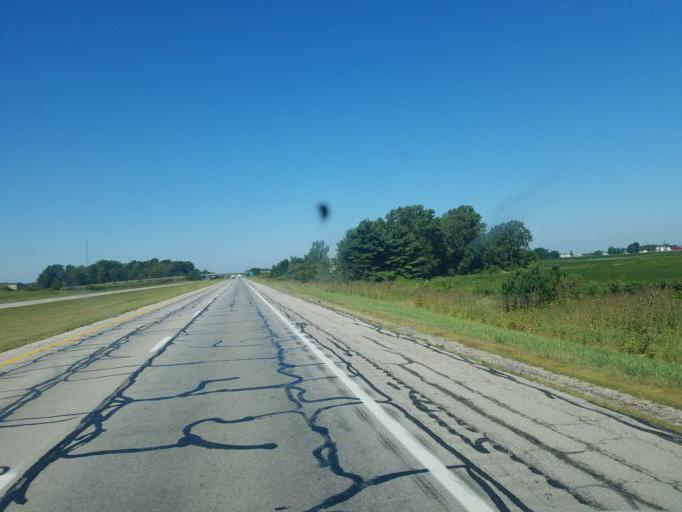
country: US
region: Ohio
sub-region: Crawford County
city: Bucyrus
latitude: 40.8274
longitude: -83.0086
